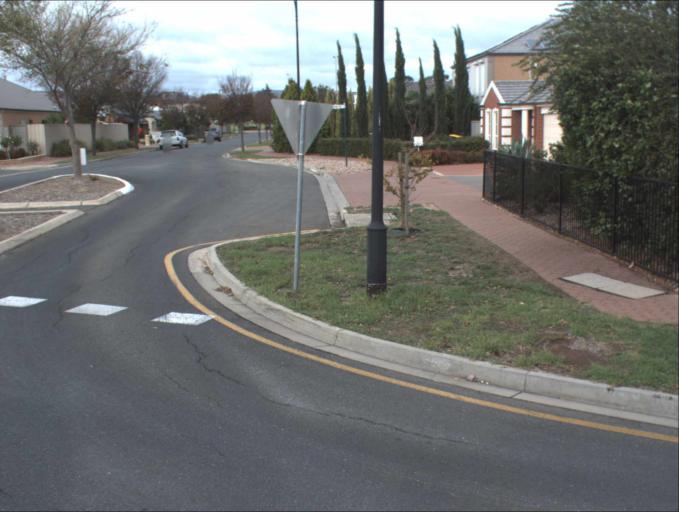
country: AU
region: South Australia
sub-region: Salisbury
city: Ingle Farm
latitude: -34.8512
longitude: 138.6300
